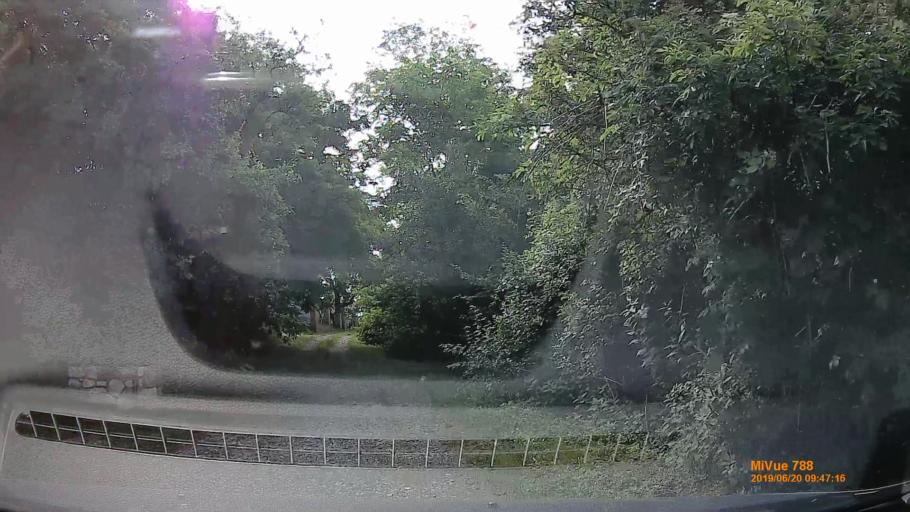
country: HU
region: Baranya
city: Pecsvarad
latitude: 46.1721
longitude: 18.4742
